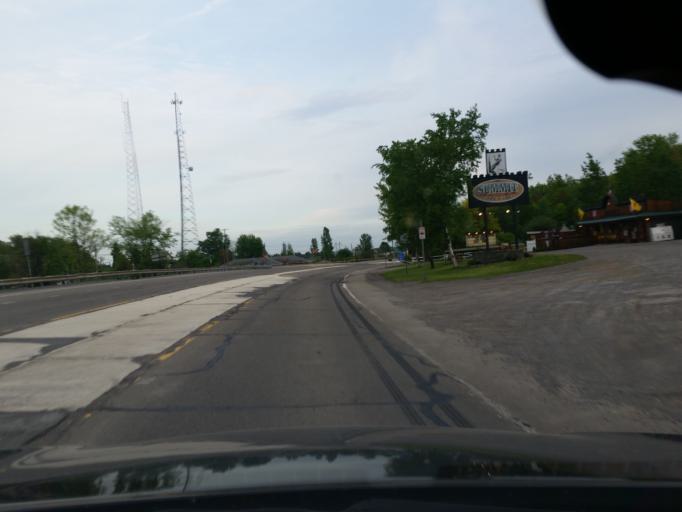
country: US
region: Pennsylvania
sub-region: Elk County
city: Ridgway
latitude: 41.3827
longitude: -78.6871
